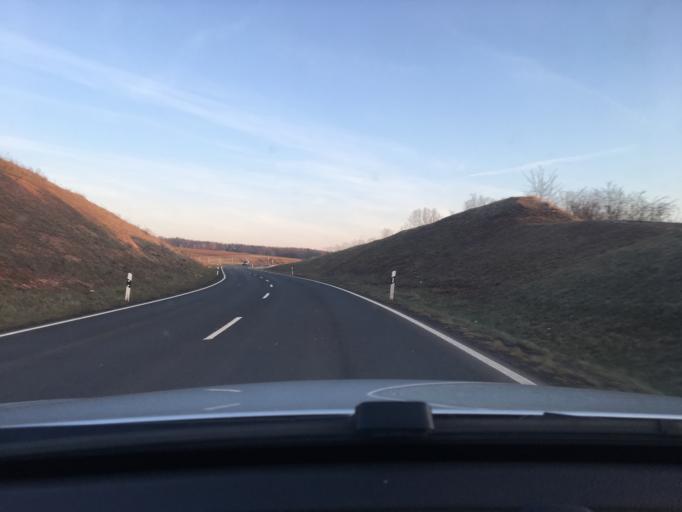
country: DE
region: Rheinland-Pfalz
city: Enkenbach-Alsenborn
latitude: 49.4866
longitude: 7.9014
